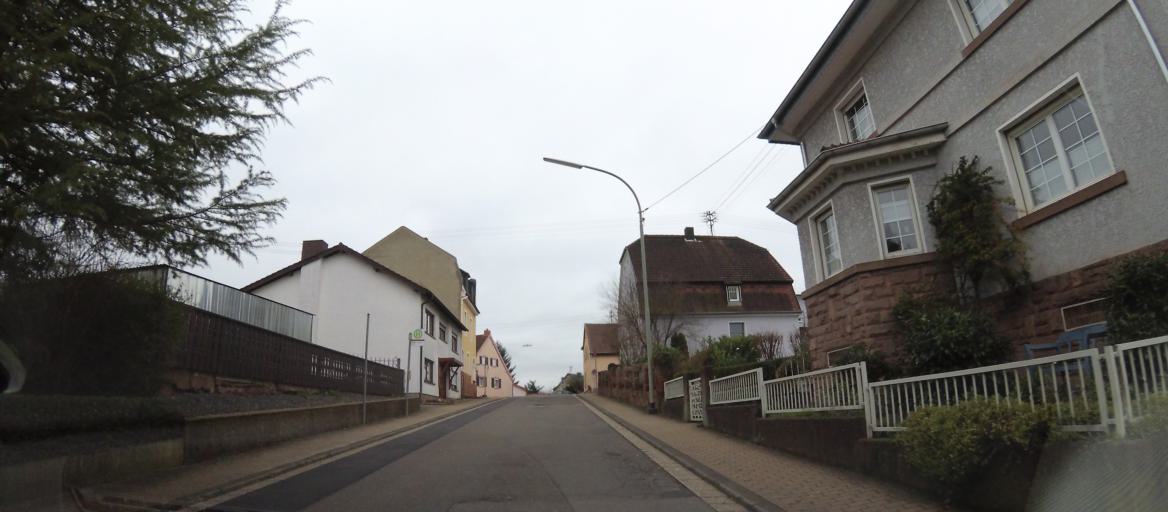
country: DE
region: Saarland
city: Illingen
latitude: 49.3745
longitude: 7.0505
